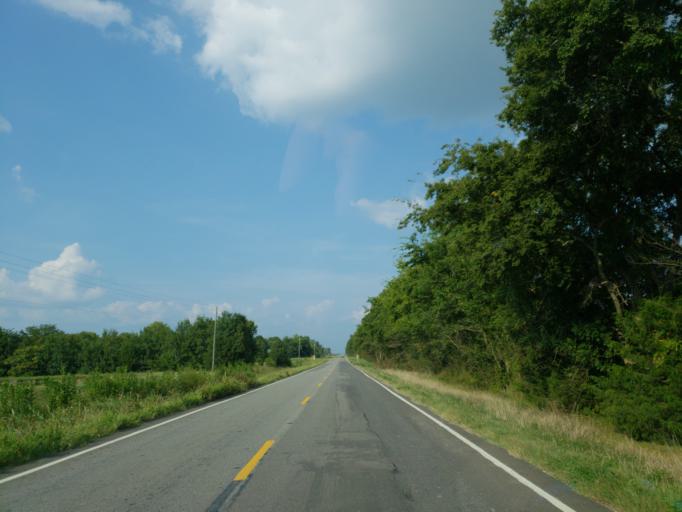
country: US
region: Alabama
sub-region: Greene County
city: Eutaw
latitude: 32.7985
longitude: -87.9637
